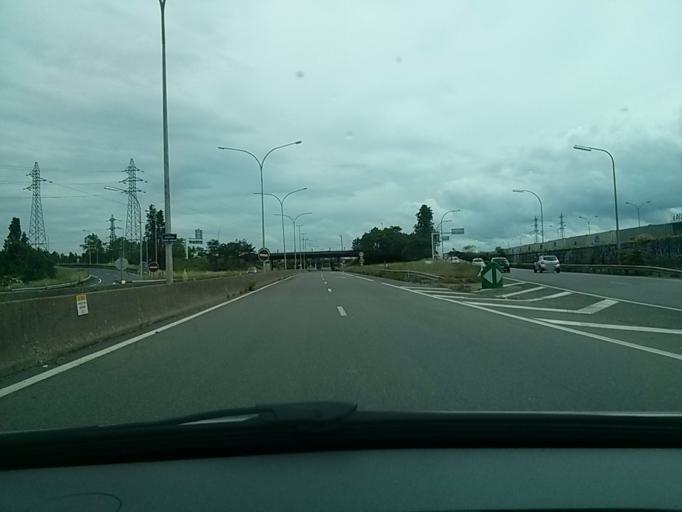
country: FR
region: Rhone-Alpes
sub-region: Departement du Rhone
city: Saint-Fons
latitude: 45.7180
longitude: 4.8425
